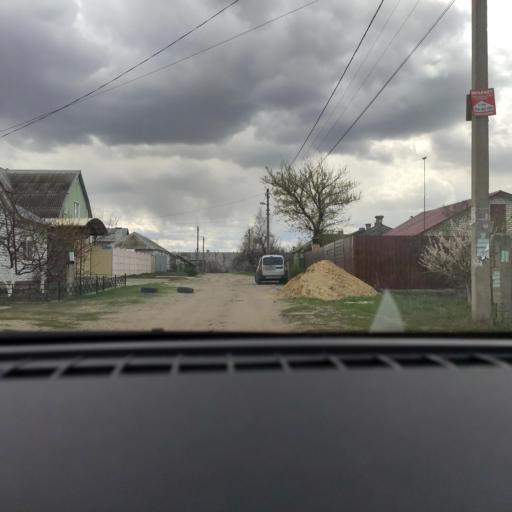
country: RU
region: Voronezj
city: Somovo
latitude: 51.7377
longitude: 39.2805
